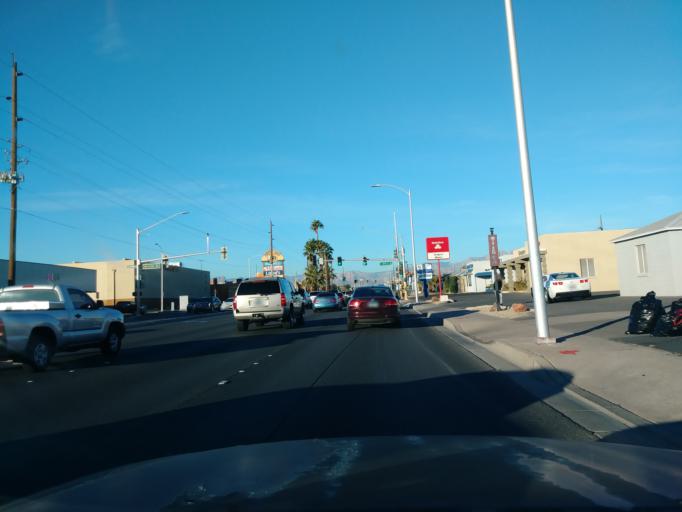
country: US
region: Nevada
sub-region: Clark County
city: Las Vegas
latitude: 36.1592
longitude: -115.1990
